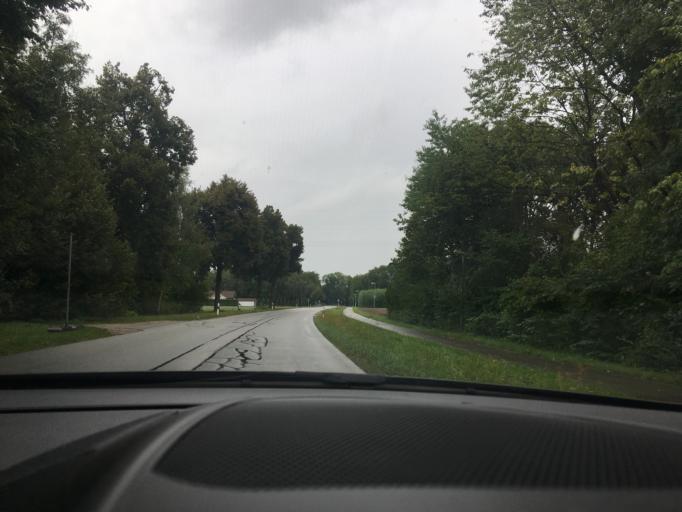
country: DE
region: Bavaria
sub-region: Upper Bavaria
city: Ismaning
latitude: 48.2441
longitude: 11.6854
